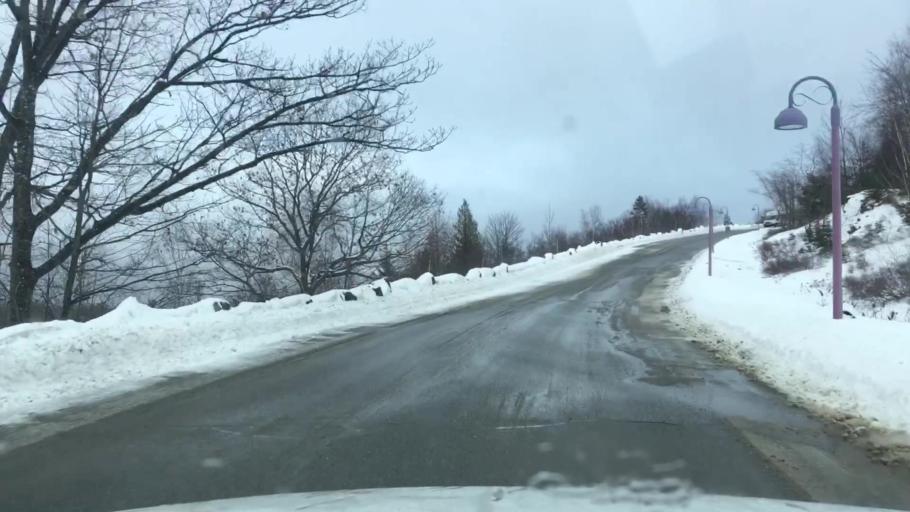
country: US
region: Maine
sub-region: Hancock County
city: Bar Harbor
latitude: 44.4149
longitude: -68.2610
